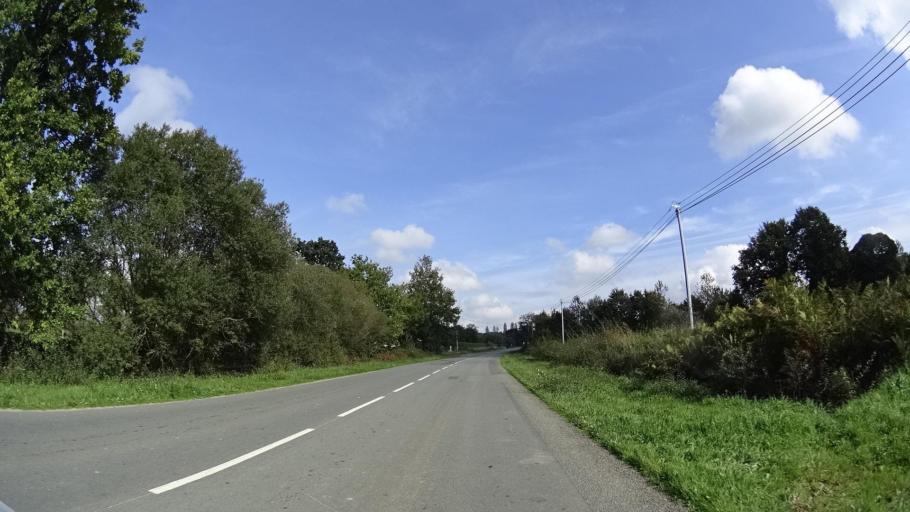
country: FR
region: Brittany
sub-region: Departement des Cotes-d'Armor
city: Plouasne
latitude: 48.2828
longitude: -1.9942
